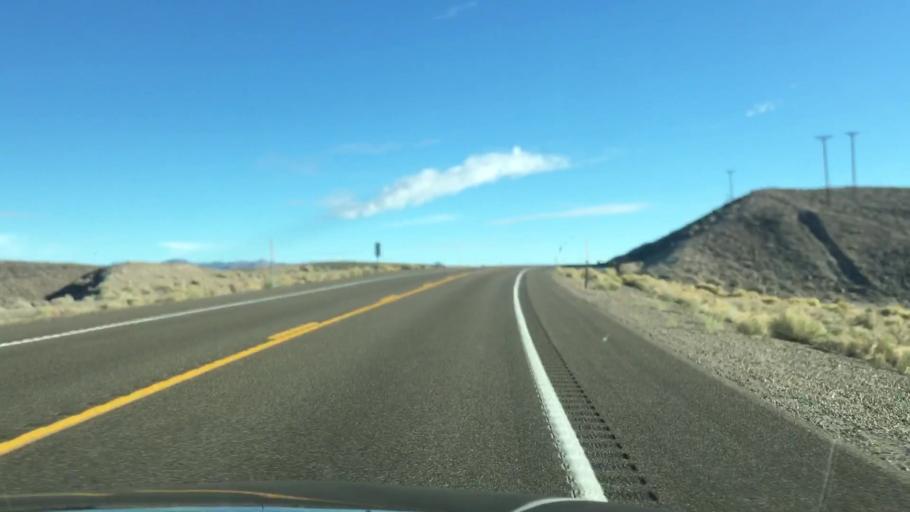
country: US
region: Nevada
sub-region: Mineral County
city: Hawthorne
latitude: 38.2186
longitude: -118.0067
